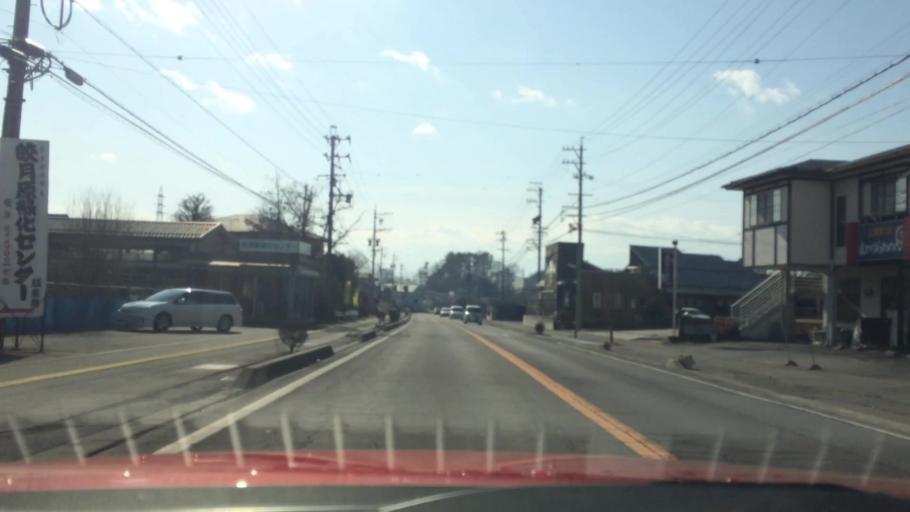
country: JP
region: Nagano
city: Komoro
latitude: 36.2937
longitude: 138.4917
